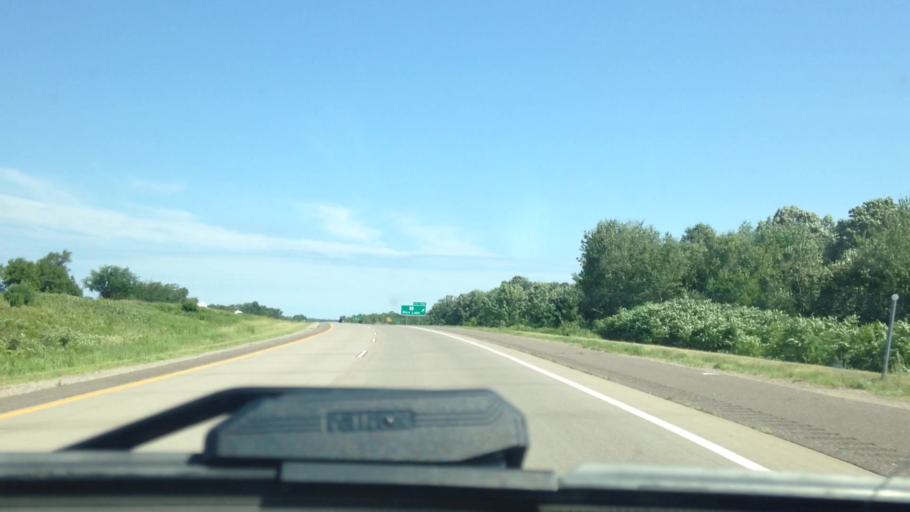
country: US
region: Wisconsin
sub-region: Barron County
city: Rice Lake
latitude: 45.4661
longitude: -91.7571
